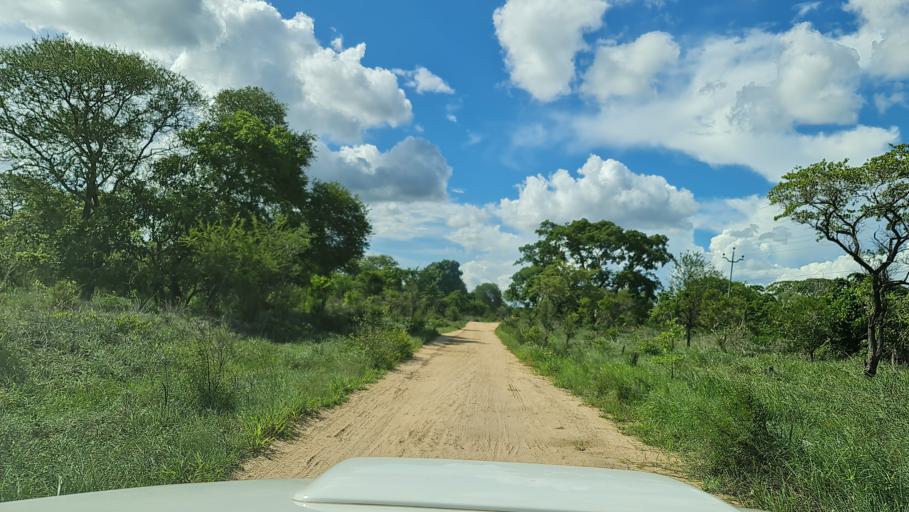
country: MZ
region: Nampula
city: Ilha de Mocambique
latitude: -15.4018
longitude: 40.2372
